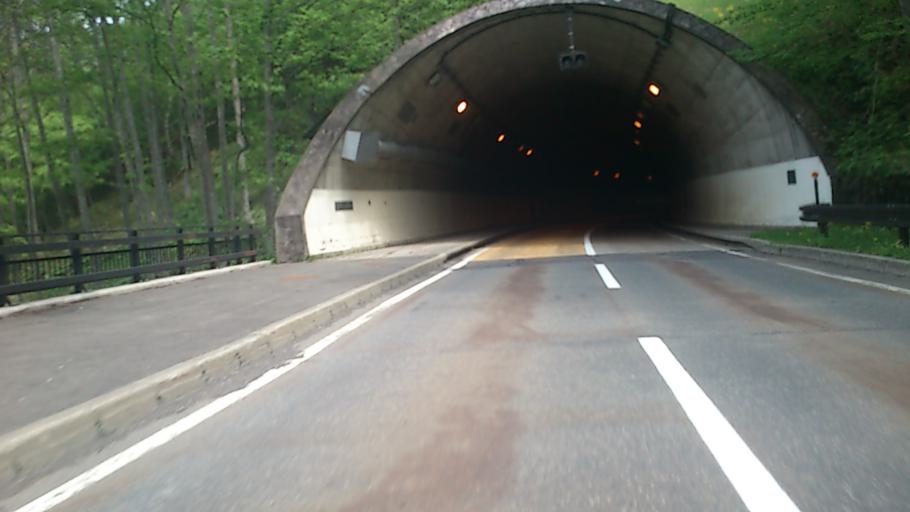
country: JP
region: Hokkaido
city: Otofuke
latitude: 43.3709
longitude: 143.2154
